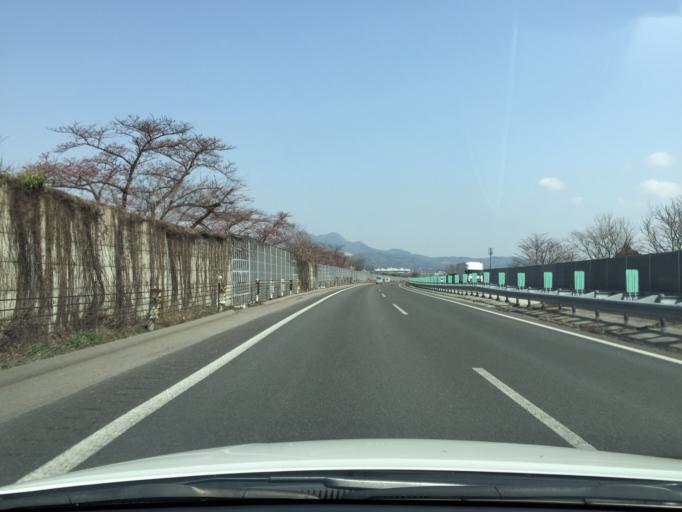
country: JP
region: Miyagi
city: Shiroishi
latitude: 37.9891
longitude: 140.6063
